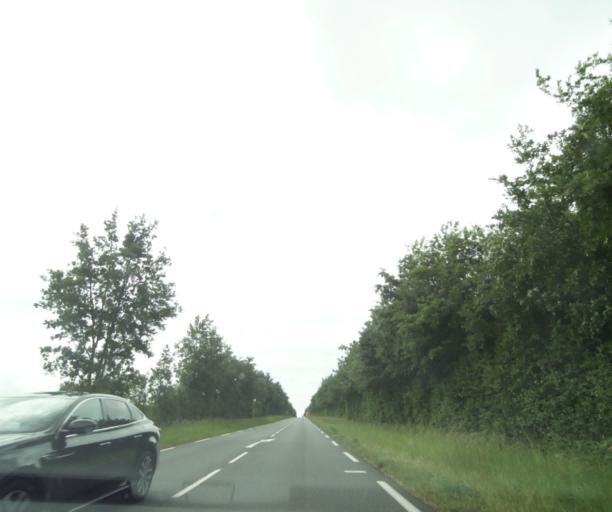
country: FR
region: Pays de la Loire
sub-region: Departement de Maine-et-Loire
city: Montreuil-Bellay
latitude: 47.1627
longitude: -0.1428
